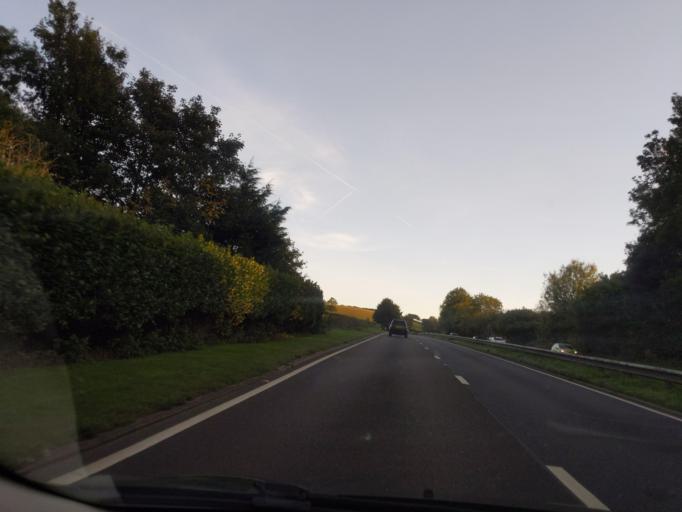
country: GB
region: England
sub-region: Devon
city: Buckfastleigh
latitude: 50.4558
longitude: -3.7907
